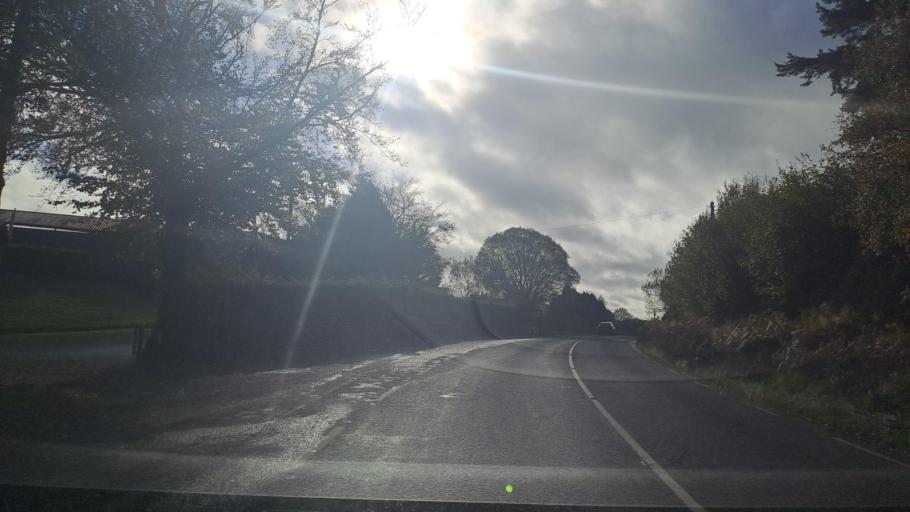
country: IE
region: Ulster
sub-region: County Monaghan
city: Monaghan
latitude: 54.2144
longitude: -6.9841
